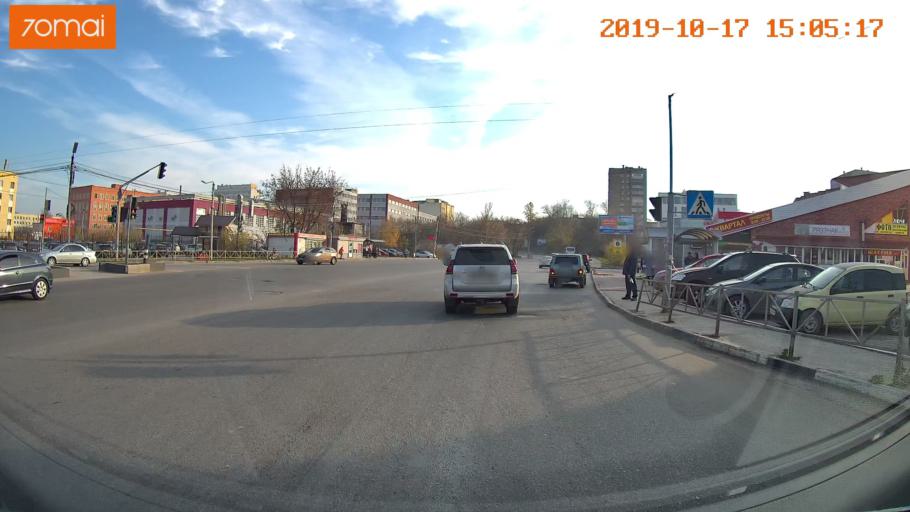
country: RU
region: Rjazan
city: Ryazan'
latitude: 54.6369
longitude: 39.7229
